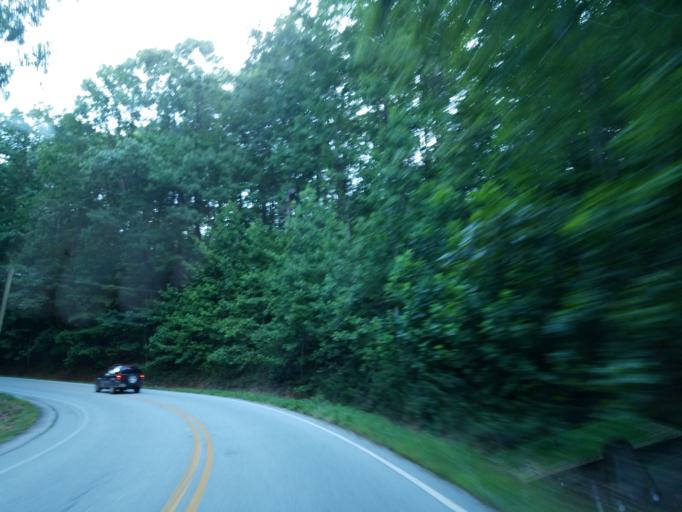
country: US
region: Georgia
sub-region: Lumpkin County
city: Dahlonega
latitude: 34.6157
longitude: -83.9620
